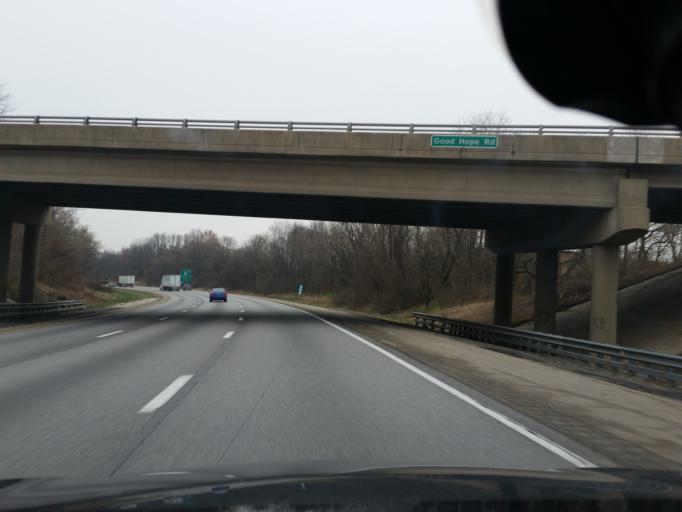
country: US
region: Pennsylvania
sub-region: Cumberland County
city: Enola
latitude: 40.2764
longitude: -76.9871
